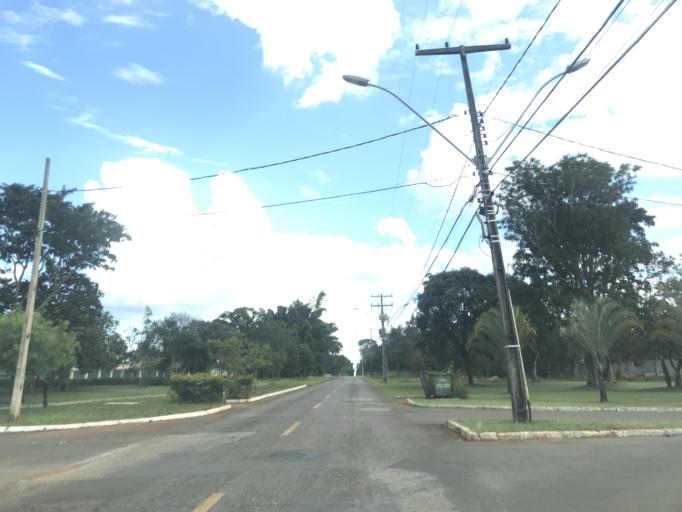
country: BR
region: Federal District
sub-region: Brasilia
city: Brasilia
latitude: -15.8986
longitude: -47.9385
